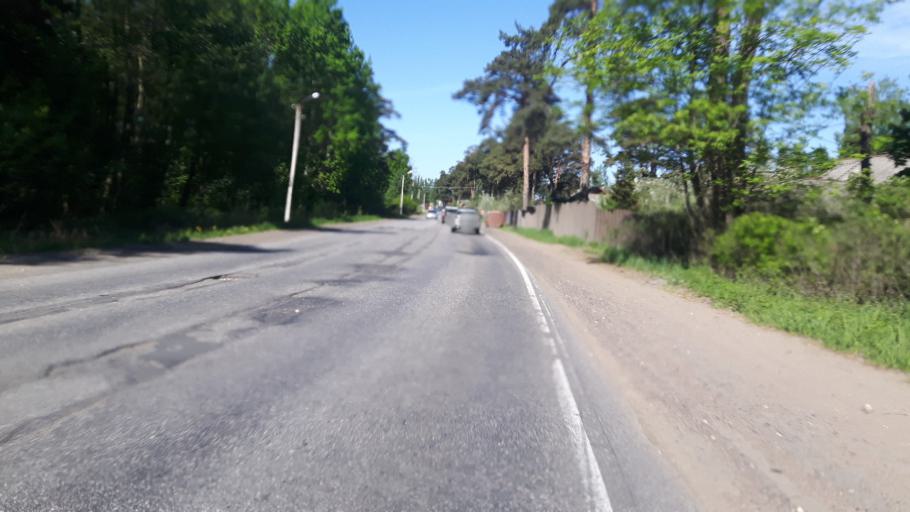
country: RU
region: Leningrad
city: Lebyazh'ye
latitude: 59.9598
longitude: 29.4370
